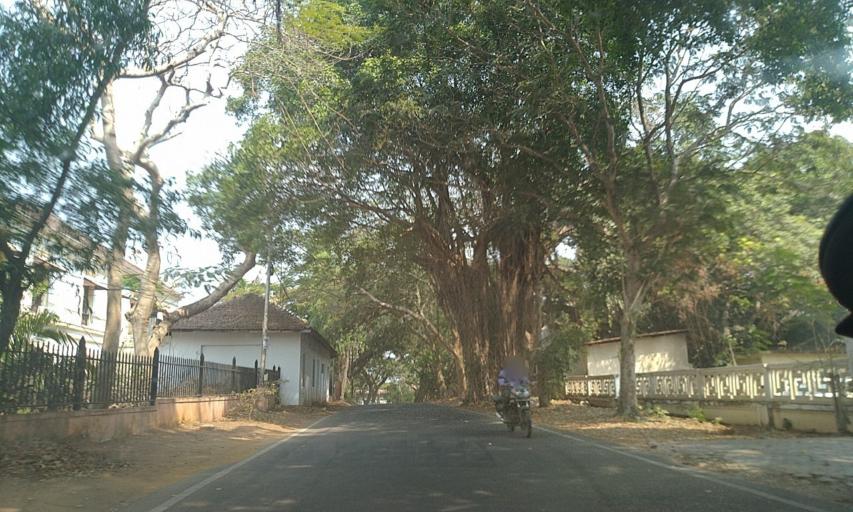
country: IN
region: Goa
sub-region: North Goa
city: Panaji
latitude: 15.4917
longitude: 73.8268
